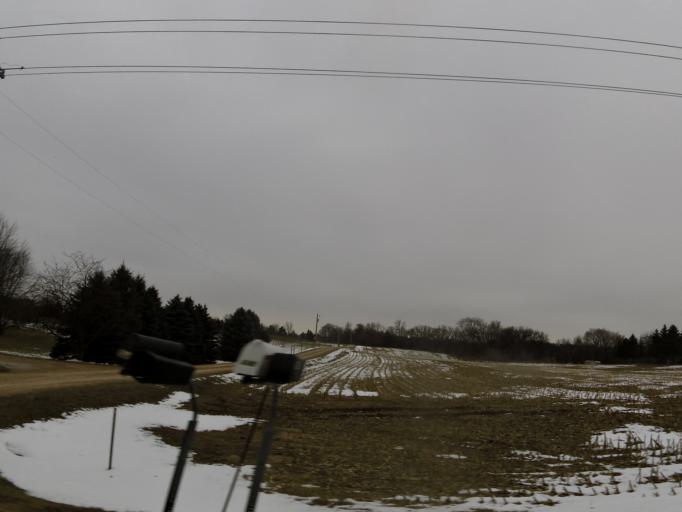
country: US
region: Minnesota
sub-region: Carver County
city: Carver
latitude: 44.7178
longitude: -93.6794
